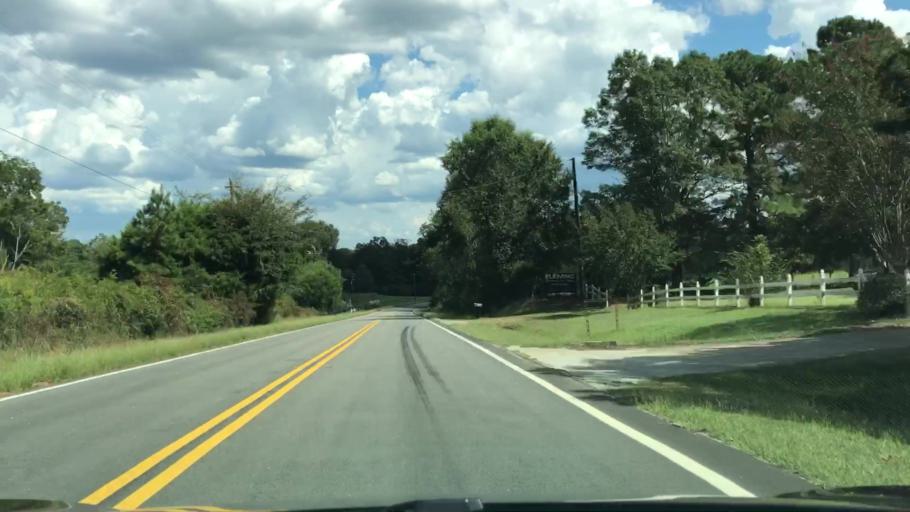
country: US
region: Georgia
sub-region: Greene County
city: Greensboro
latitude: 33.5657
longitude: -83.1505
